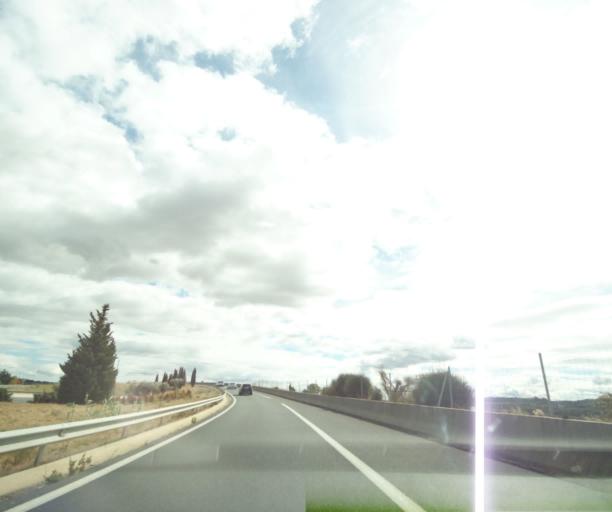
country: FR
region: Languedoc-Roussillon
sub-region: Departement de l'Herault
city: Nebian
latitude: 43.6564
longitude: 3.4457
